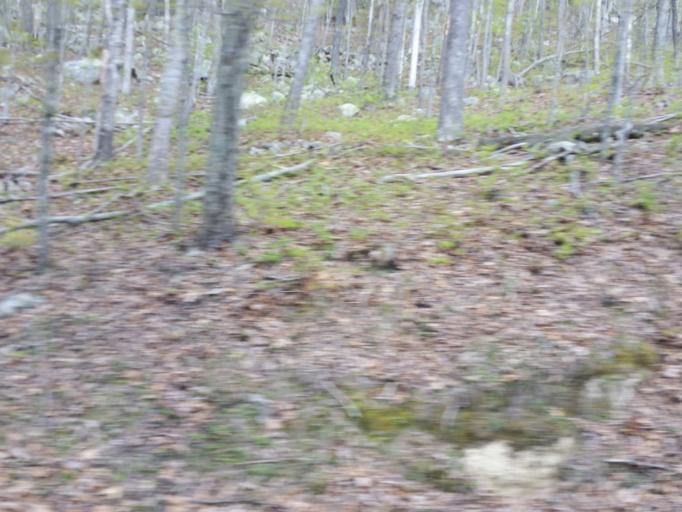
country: US
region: Tennessee
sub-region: Claiborne County
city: Harrogate
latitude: 36.6082
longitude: -83.6760
